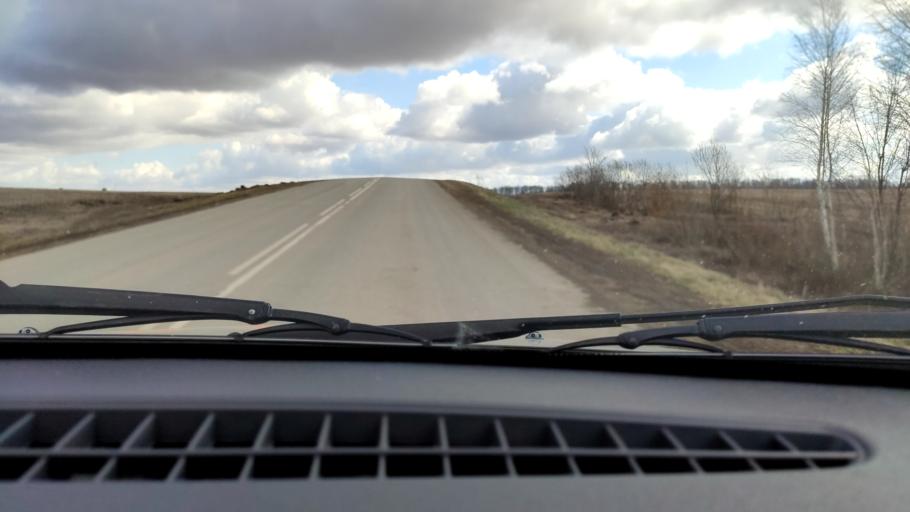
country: RU
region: Bashkortostan
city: Iglino
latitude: 54.8768
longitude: 56.5302
